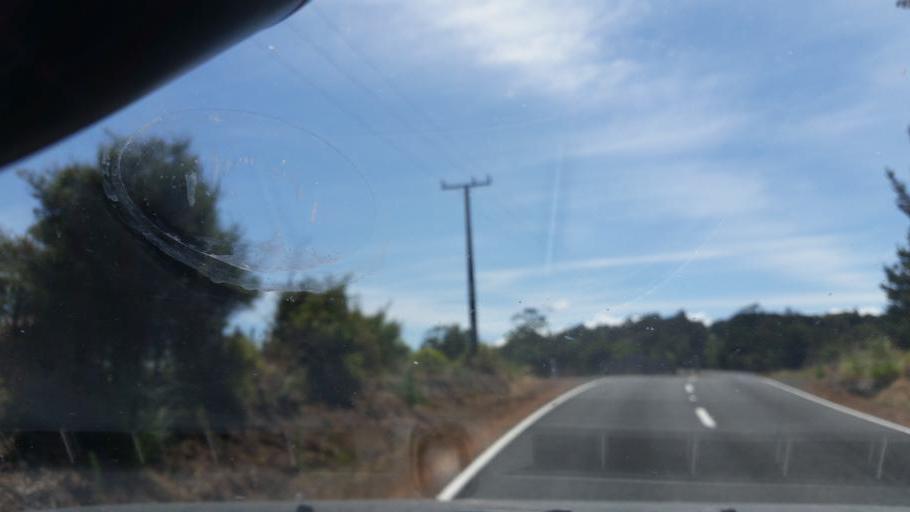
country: NZ
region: Auckland
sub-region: Auckland
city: Wellsford
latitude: -36.2316
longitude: 174.2131
